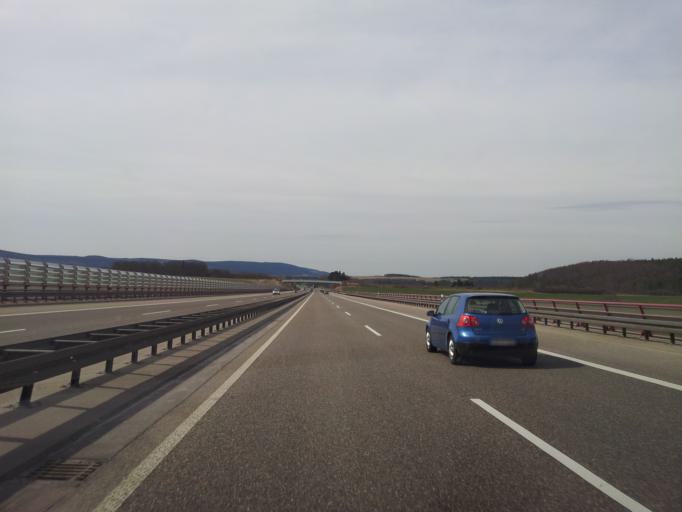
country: DE
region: Thuringia
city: Martinroda
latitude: 50.7187
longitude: 10.8697
